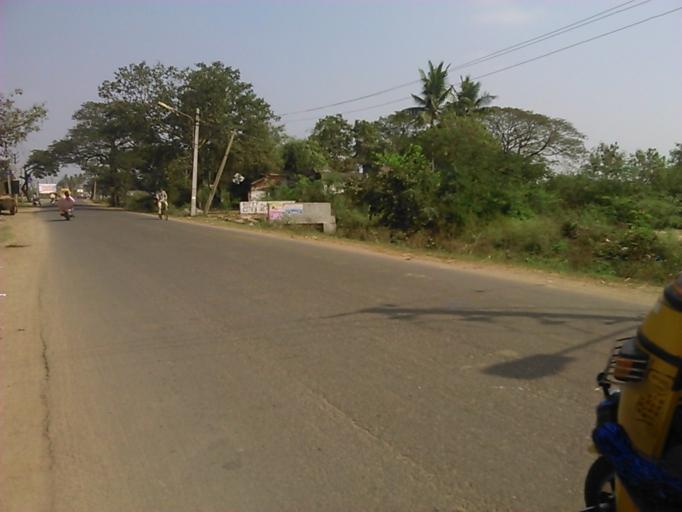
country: IN
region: Andhra Pradesh
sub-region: Guntur
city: Bhattiprolu
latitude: 16.2377
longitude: 80.6621
